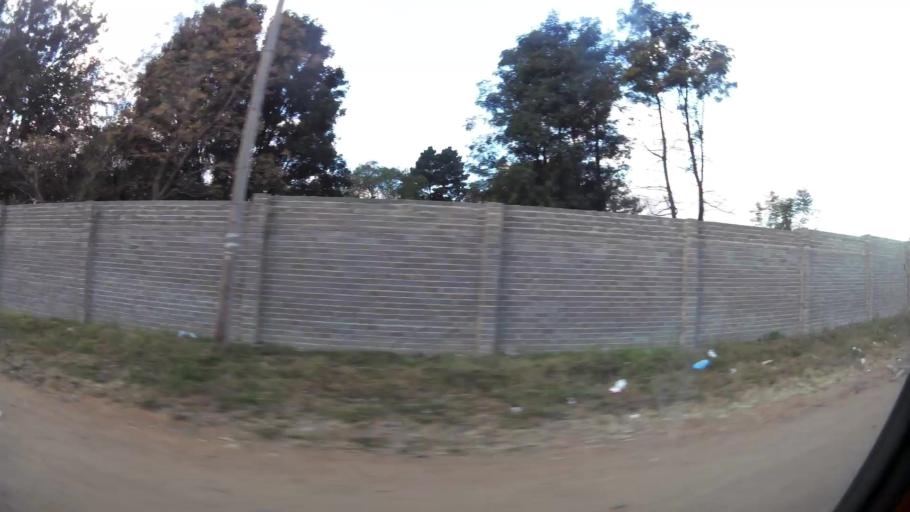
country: ZA
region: Gauteng
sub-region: City of Johannesburg Metropolitan Municipality
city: Midrand
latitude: -26.0091
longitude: 28.1604
